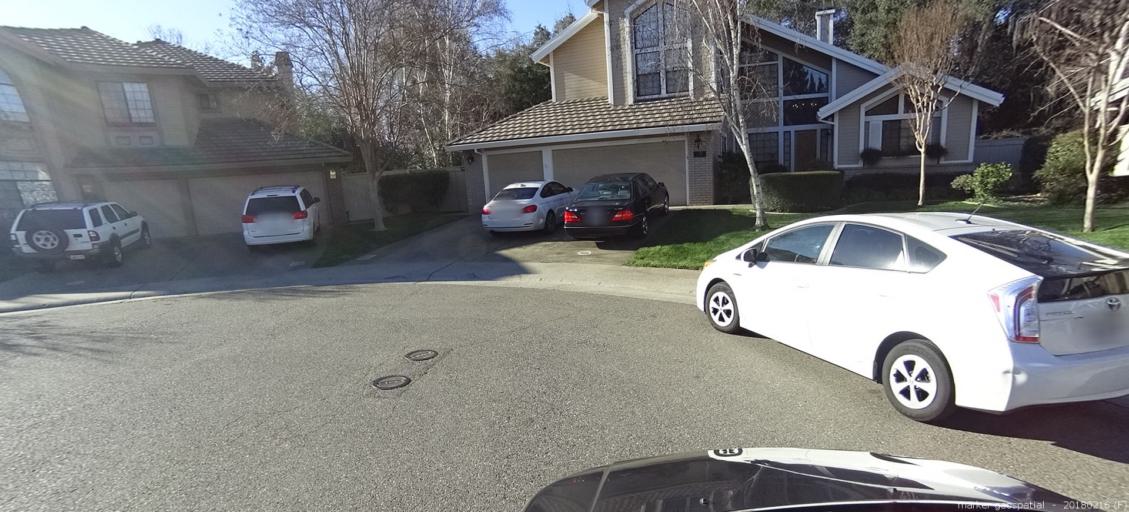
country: US
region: California
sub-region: Sacramento County
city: Gold River
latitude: 38.6244
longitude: -121.2424
